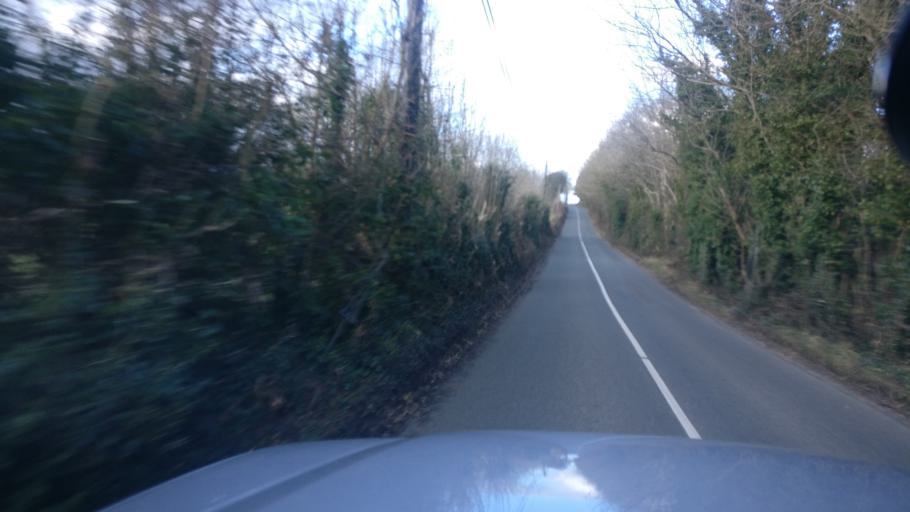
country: IE
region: Connaught
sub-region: County Galway
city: Loughrea
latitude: 53.2168
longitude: -8.3962
